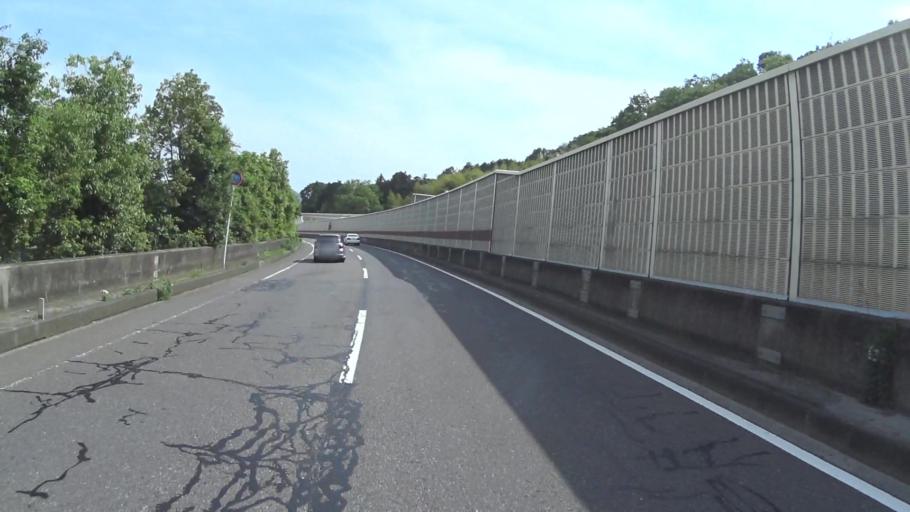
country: JP
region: Shiga Prefecture
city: Otsu-shi
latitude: 35.0397
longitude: 135.8529
